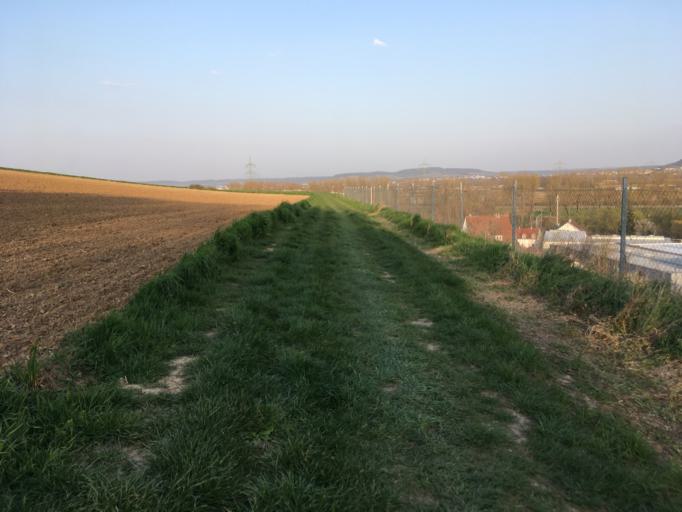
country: DE
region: Baden-Wuerttemberg
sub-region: Regierungsbezirk Stuttgart
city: Nordheim
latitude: 49.1094
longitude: 9.1450
